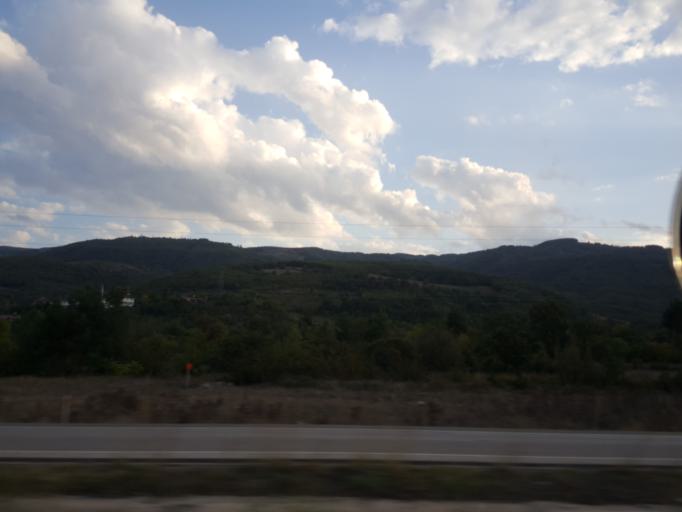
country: TR
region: Tokat
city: Niksar
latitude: 40.4898
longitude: 36.9527
